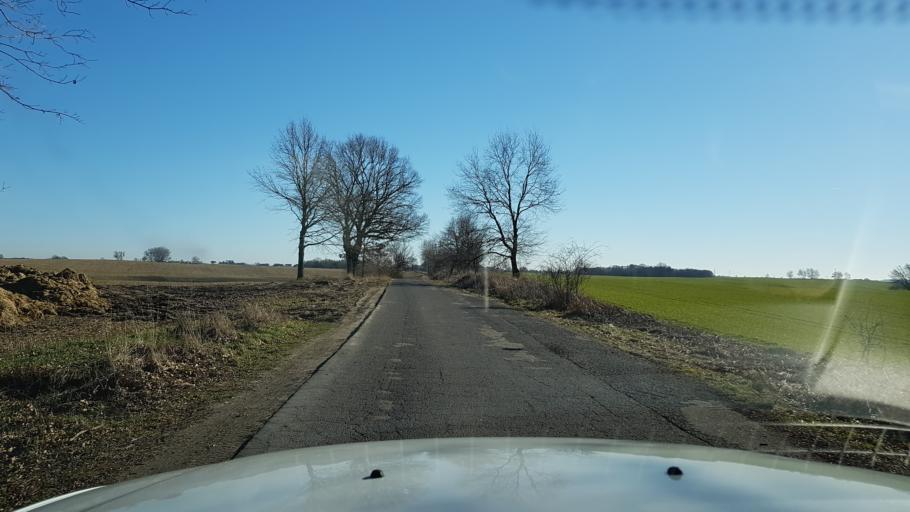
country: PL
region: West Pomeranian Voivodeship
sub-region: Powiat mysliborski
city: Barlinek
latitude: 53.0122
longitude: 15.1380
